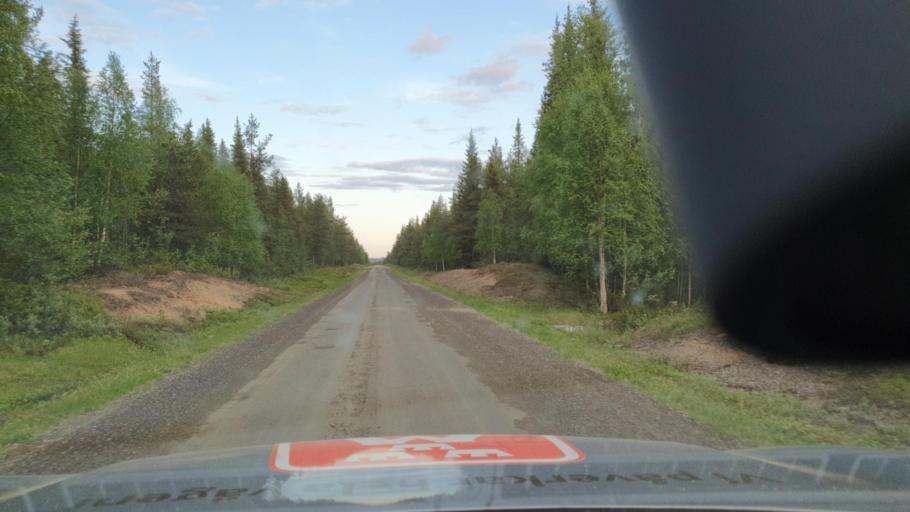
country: SE
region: Norrbotten
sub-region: Bodens Kommun
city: Boden
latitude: 66.5903
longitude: 21.3829
